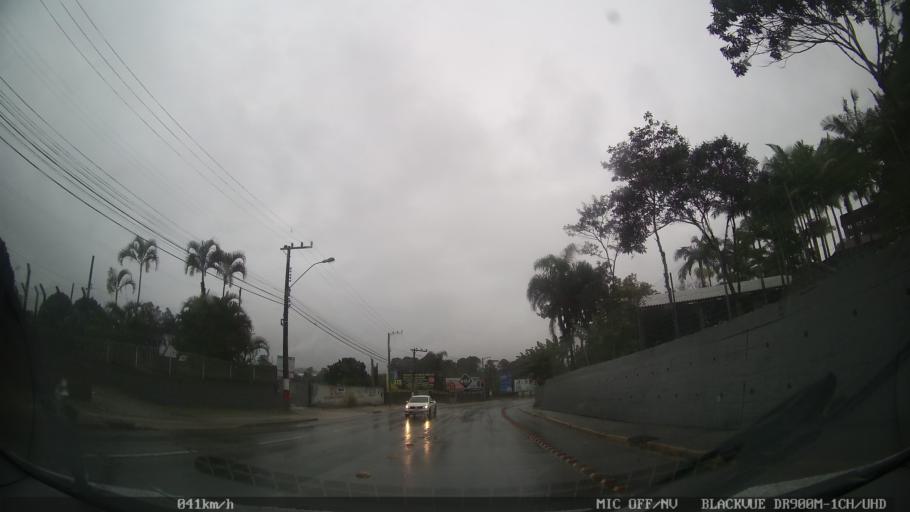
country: BR
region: Santa Catarina
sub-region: Balneario Camboriu
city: Balneario Camboriu
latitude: -27.0126
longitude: -48.6479
